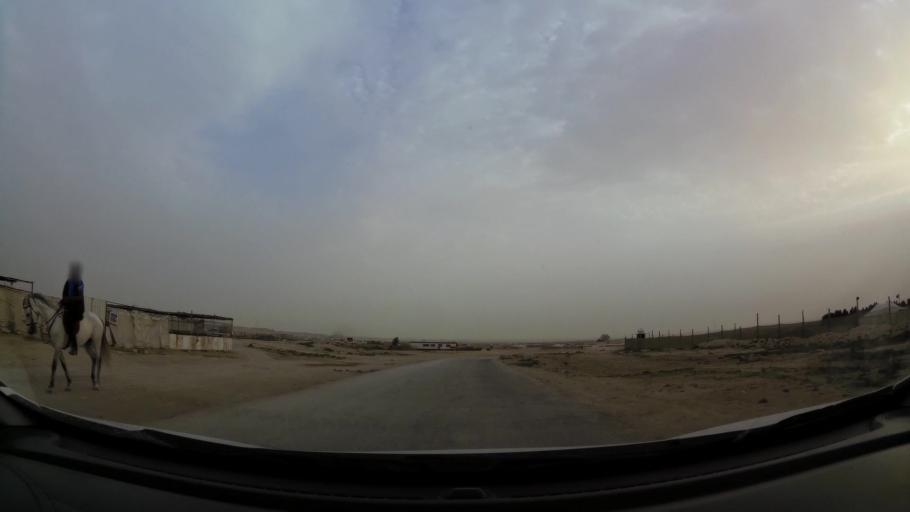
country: BH
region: Central Governorate
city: Dar Kulayb
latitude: 26.0006
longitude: 50.5852
